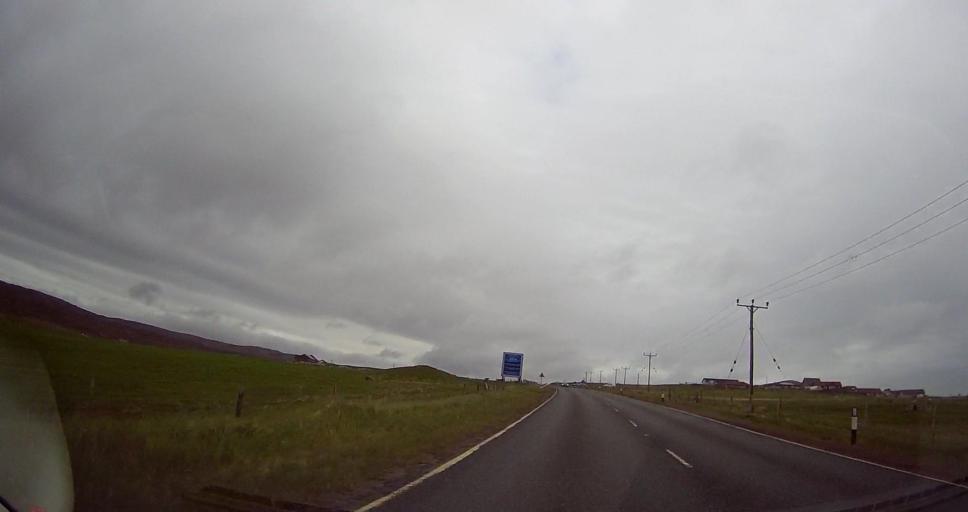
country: GB
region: Scotland
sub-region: Shetland Islands
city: Lerwick
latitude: 60.1961
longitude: -1.2320
